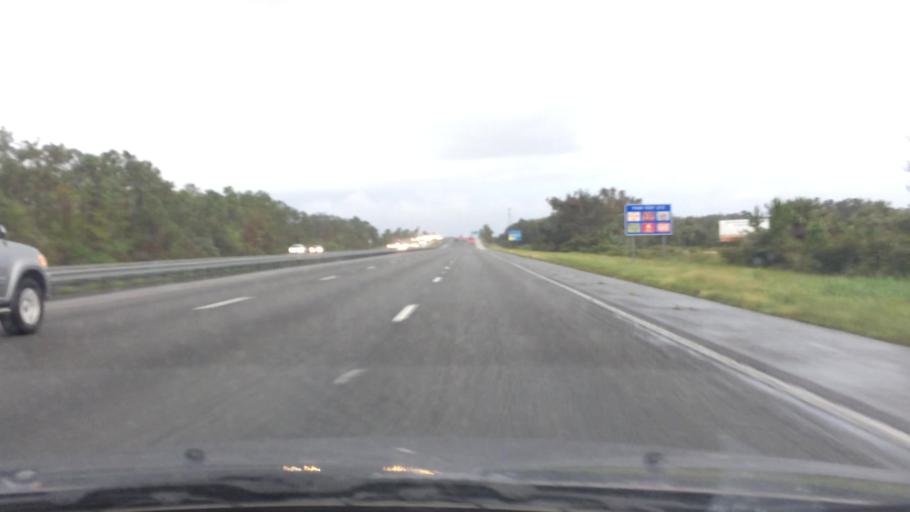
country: US
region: Florida
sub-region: Volusia County
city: Ormond-by-the-Sea
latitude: 29.3271
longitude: -81.1312
